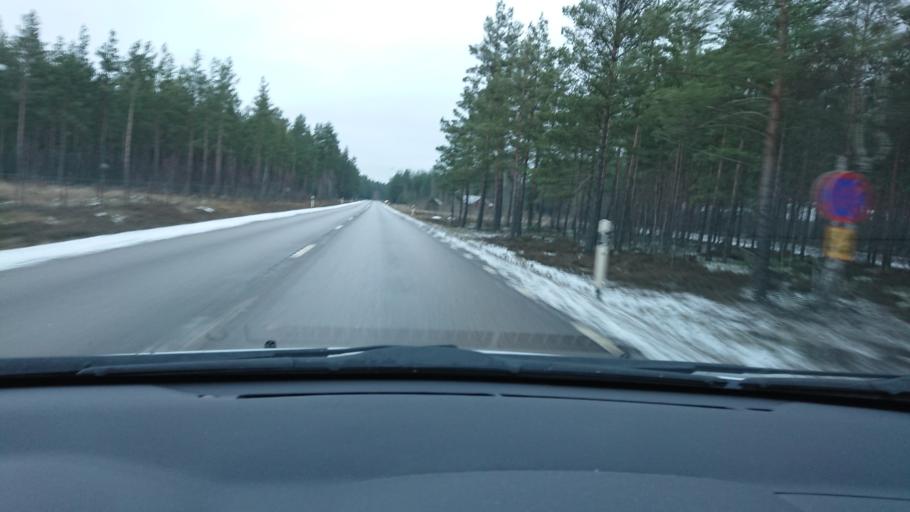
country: SE
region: Kalmar
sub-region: Hultsfreds Kommun
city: Hultsfred
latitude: 57.5226
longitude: 15.8443
